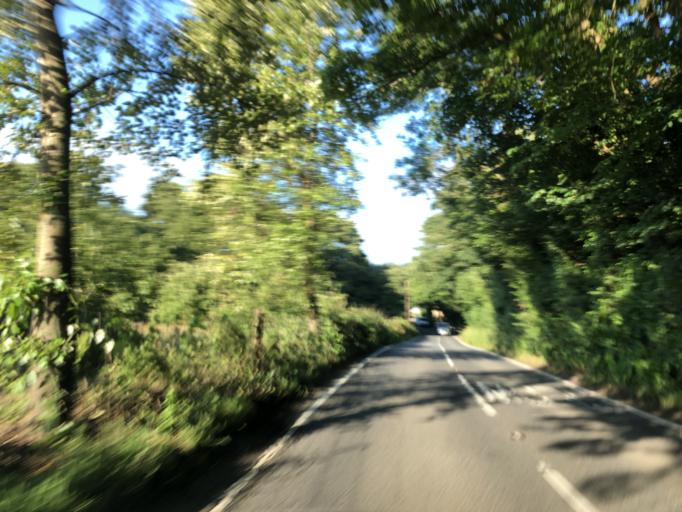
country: GB
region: England
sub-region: Isle of Wight
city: Shalfleet
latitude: 50.6790
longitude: -1.4119
